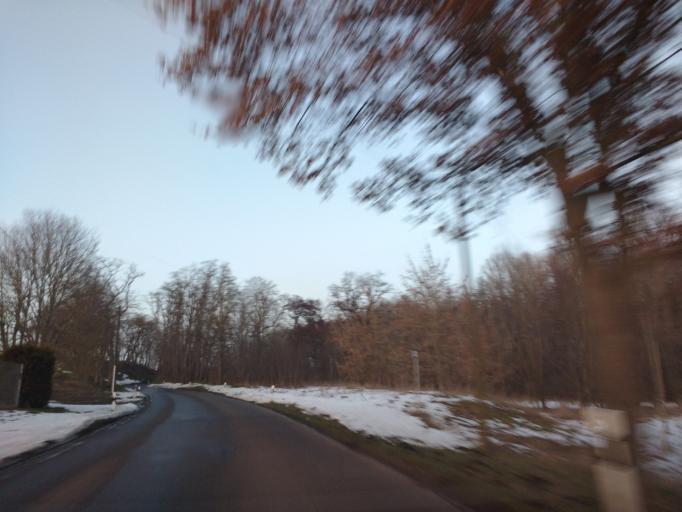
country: DE
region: Saxony-Anhalt
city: Gutenberg
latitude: 51.5505
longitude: 11.9782
